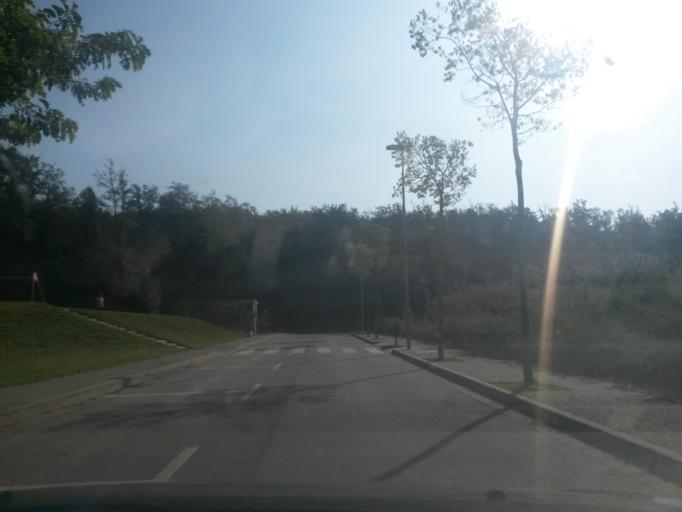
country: ES
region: Catalonia
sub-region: Provincia de Girona
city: Fornells de la Selva
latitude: 41.9524
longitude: 2.8086
